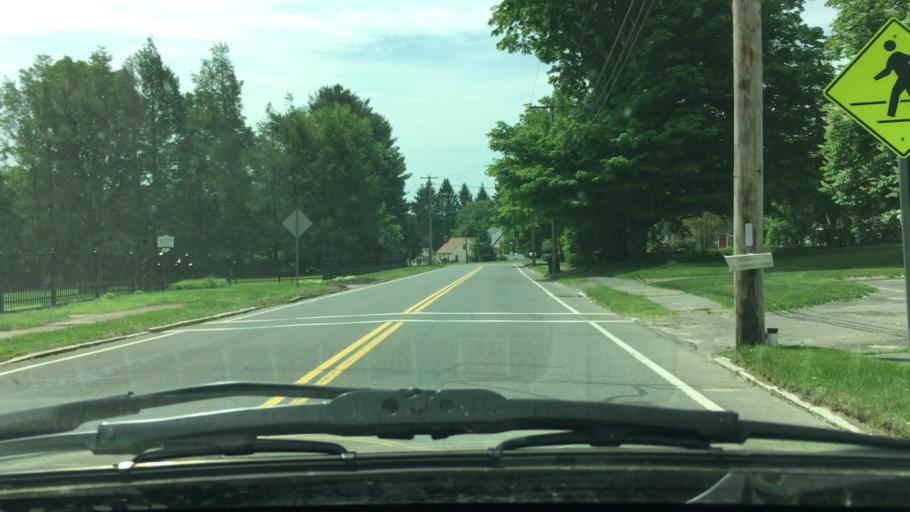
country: US
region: Massachusetts
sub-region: Hampshire County
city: Belchertown
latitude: 42.2723
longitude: -72.3982
